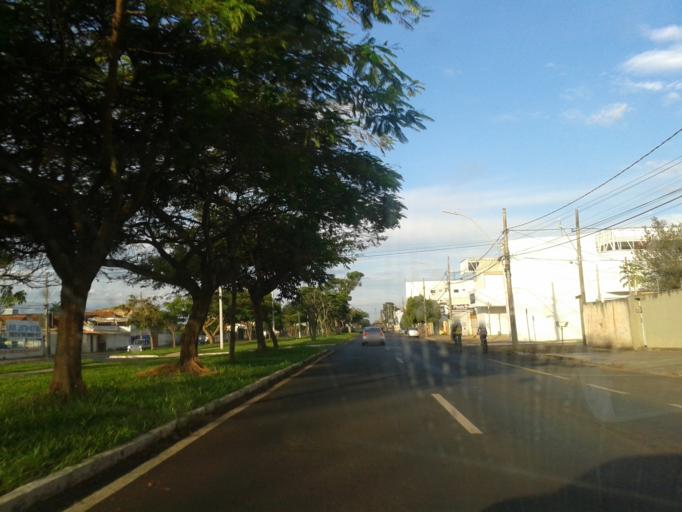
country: BR
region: Minas Gerais
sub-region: Araguari
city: Araguari
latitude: -18.6407
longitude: -48.1899
